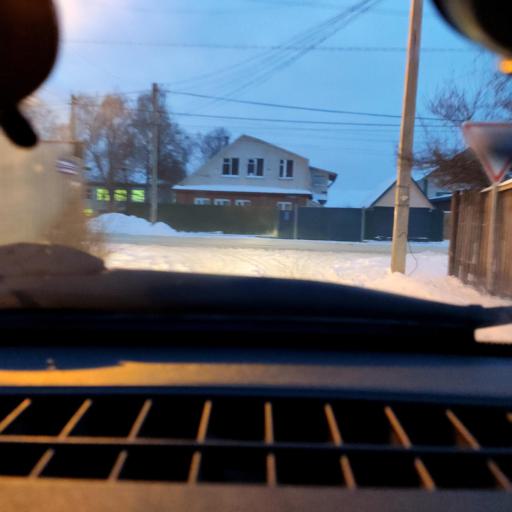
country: RU
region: Bashkortostan
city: Mikhaylovka
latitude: 54.8051
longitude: 55.8872
